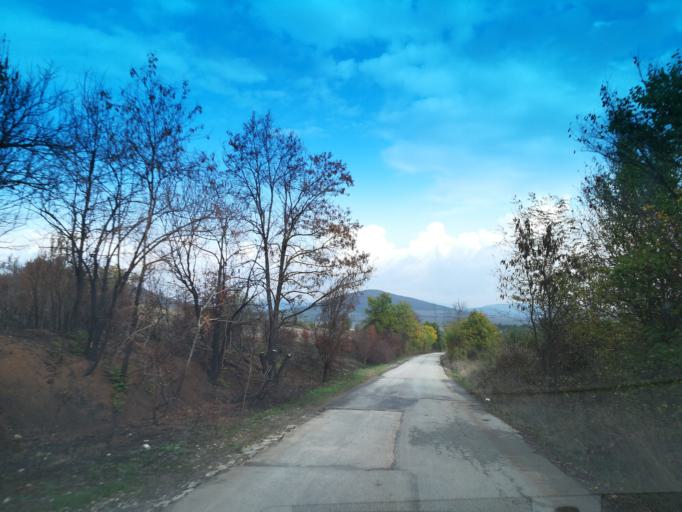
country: BG
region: Stara Zagora
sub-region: Obshtina Nikolaevo
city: Elkhovo
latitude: 42.3336
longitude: 25.4044
